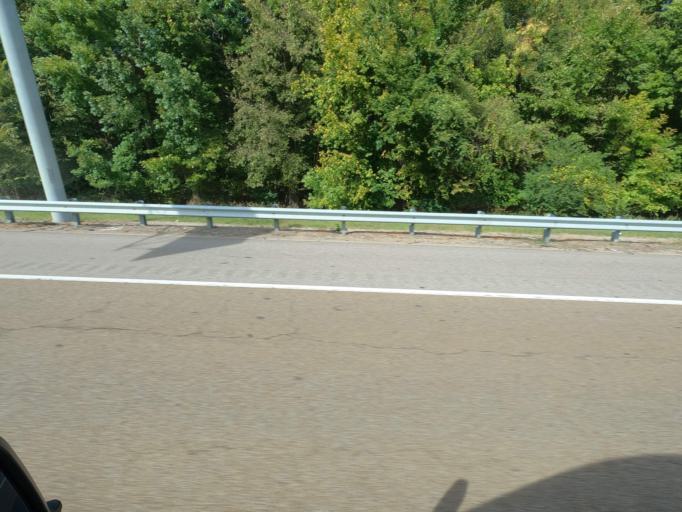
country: US
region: Tennessee
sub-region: Shelby County
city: Lakeland
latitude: 35.1981
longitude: -89.7858
